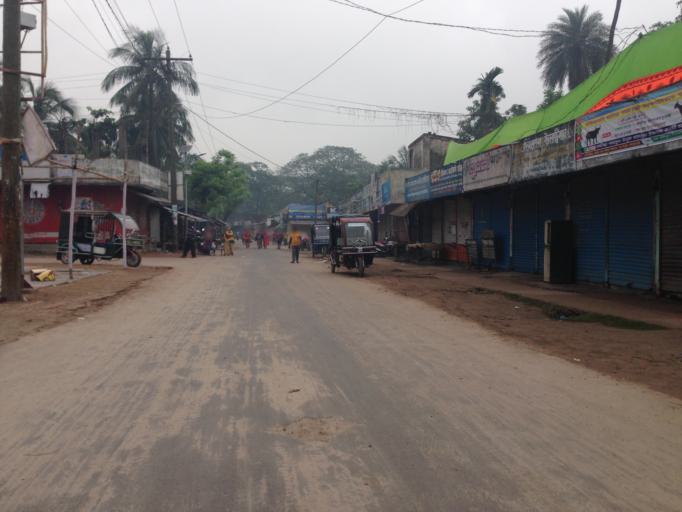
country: BD
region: Khulna
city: Kalia
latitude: 23.0378
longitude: 89.6325
